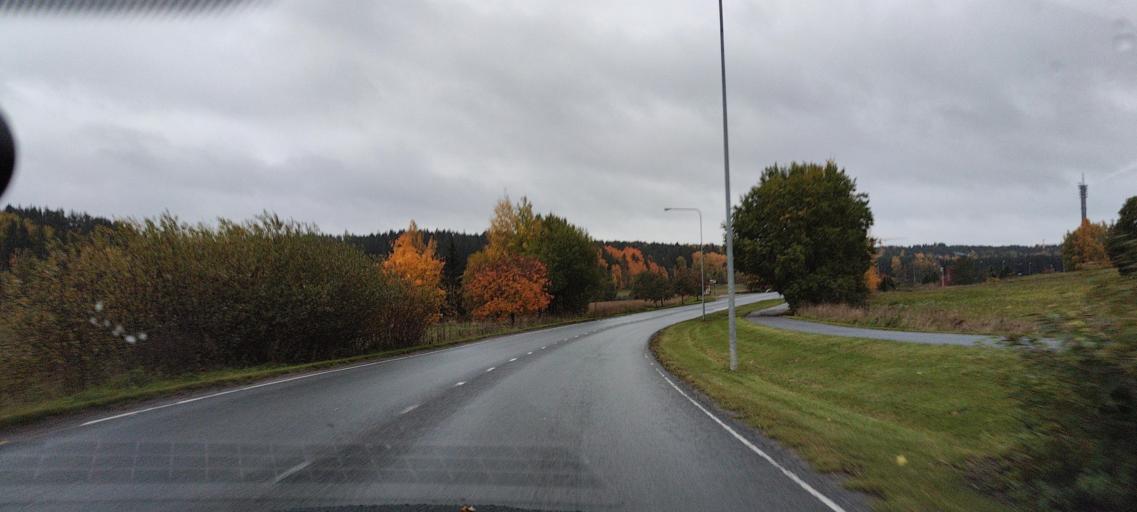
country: FI
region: Varsinais-Suomi
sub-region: Turku
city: Kaarina
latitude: 60.4605
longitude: 22.3347
